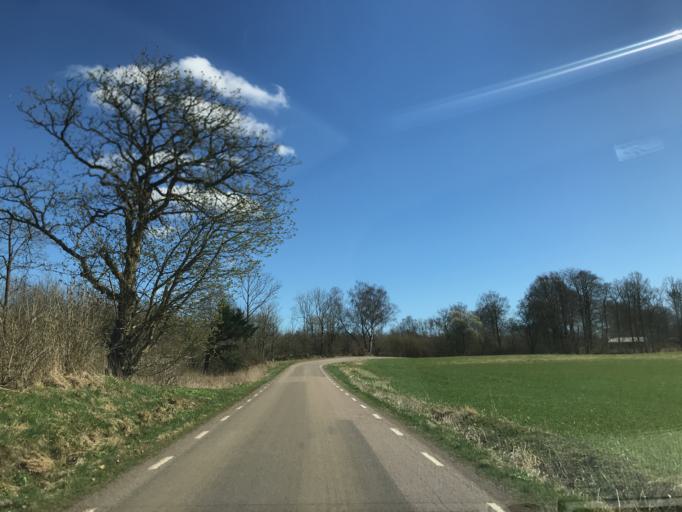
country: SE
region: Skane
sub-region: Svalovs Kommun
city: Kagerod
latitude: 56.0359
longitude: 13.1592
